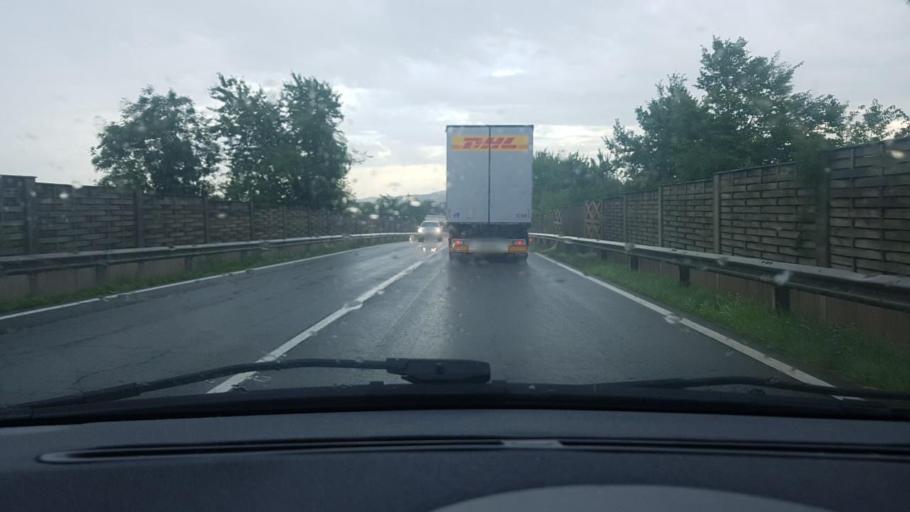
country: AT
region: Styria
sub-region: Politischer Bezirk Graz-Umgebung
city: Kalsdorf bei Graz
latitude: 46.9720
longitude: 15.4675
